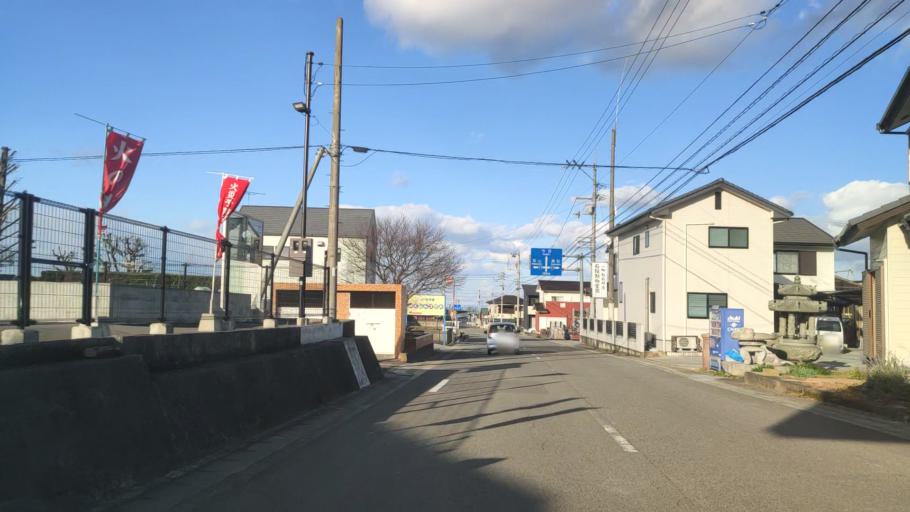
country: JP
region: Ehime
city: Saijo
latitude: 33.8930
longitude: 133.1320
